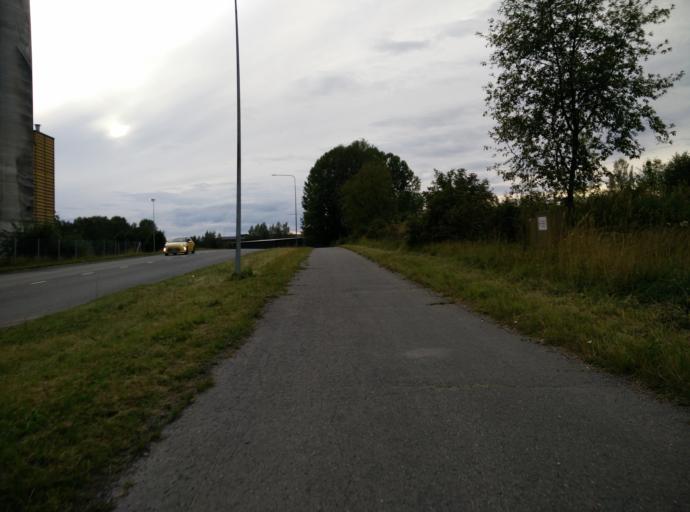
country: FI
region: Haeme
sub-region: Haemeenlinna
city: Haemeenlinna
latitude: 60.9828
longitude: 24.4989
